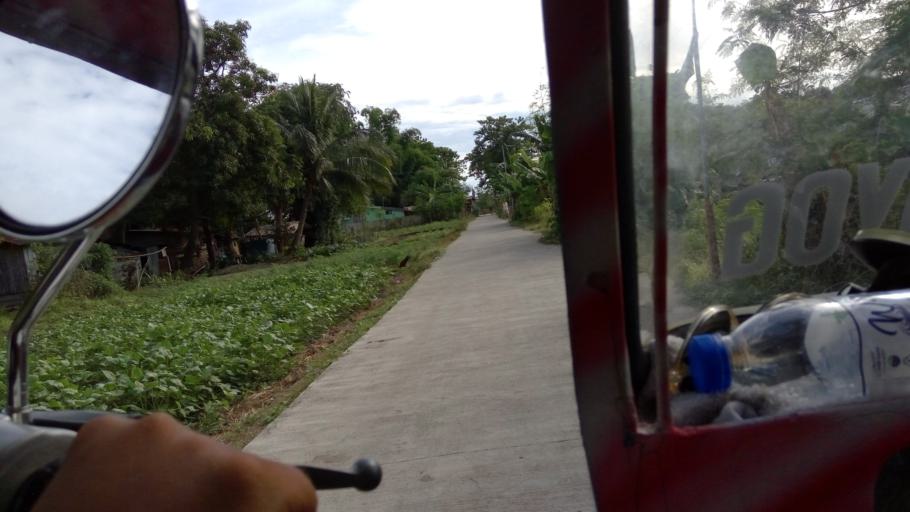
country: PH
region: Ilocos
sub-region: Province of La Union
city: San Eugenio
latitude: 16.3660
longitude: 120.3524
